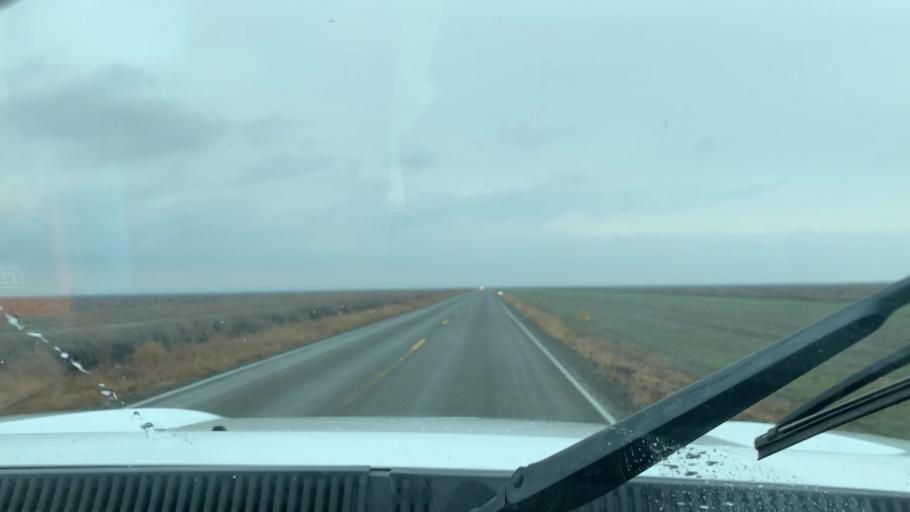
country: US
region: California
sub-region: Kings County
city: Corcoran
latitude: 35.9339
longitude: -119.7110
